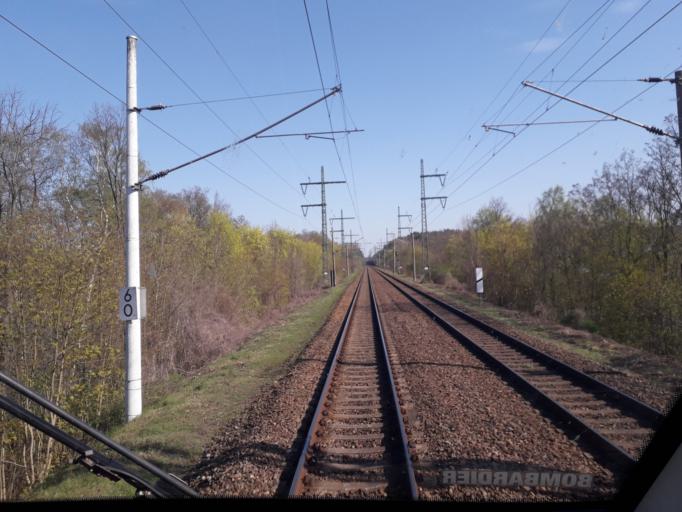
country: DE
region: Brandenburg
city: Potsdam
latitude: 52.3672
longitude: 13.0222
